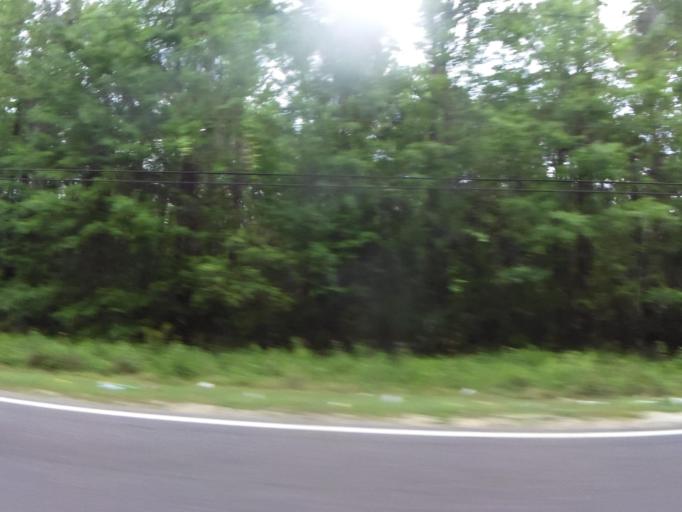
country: US
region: Florida
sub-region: Clay County
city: Bellair-Meadowbrook Terrace
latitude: 30.2009
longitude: -81.7290
